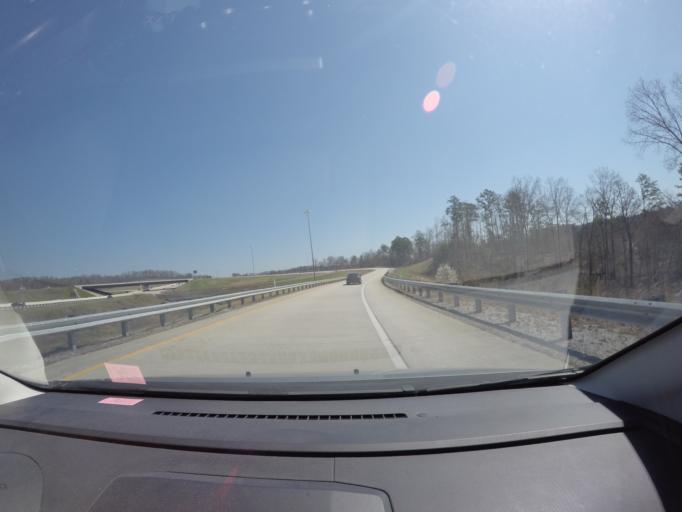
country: US
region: Tennessee
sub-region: Hamilton County
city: Harrison
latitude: 35.0721
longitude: -85.1143
